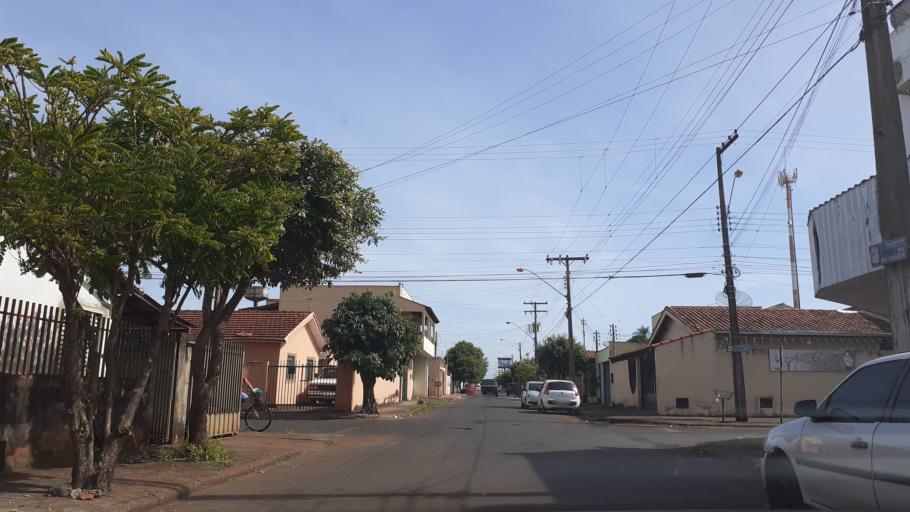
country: BR
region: Goias
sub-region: Itumbiara
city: Itumbiara
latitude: -18.4148
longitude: -49.2347
